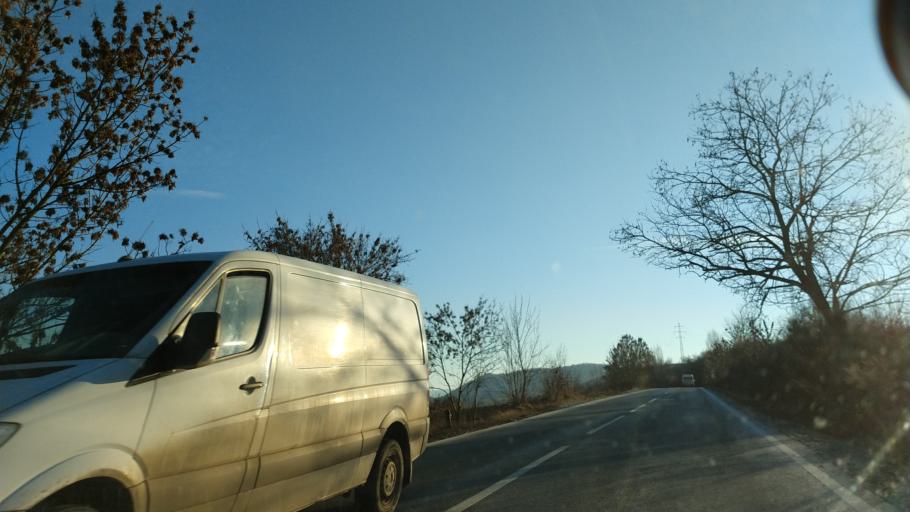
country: RO
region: Bacau
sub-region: Comuna Helegiu
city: Bratila
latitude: 46.2988
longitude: 26.7524
